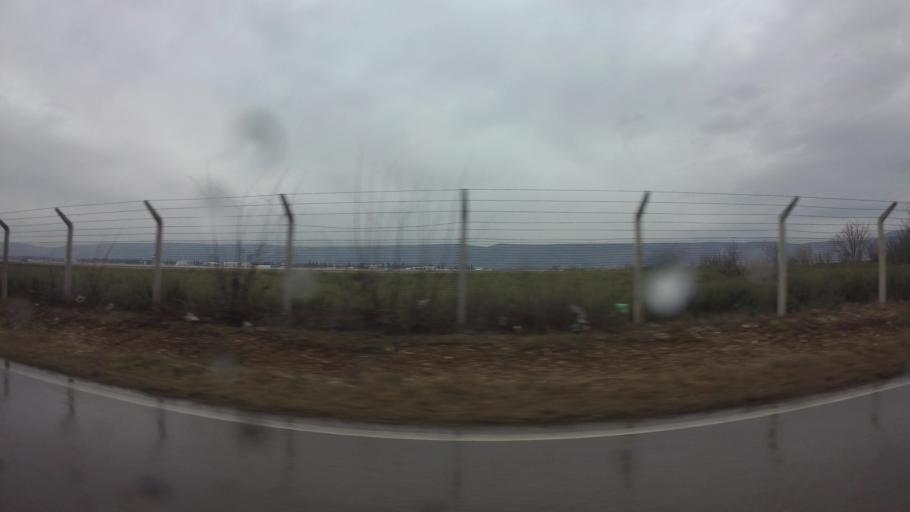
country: BA
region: Federation of Bosnia and Herzegovina
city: Rodoc
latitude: 43.2939
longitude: 17.8445
